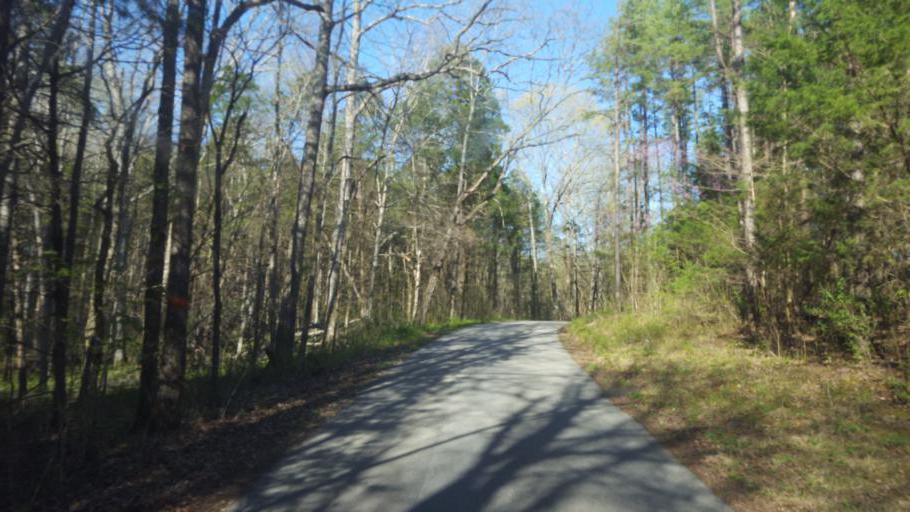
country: US
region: Kentucky
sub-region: Barren County
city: Cave City
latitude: 37.2030
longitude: -86.0305
